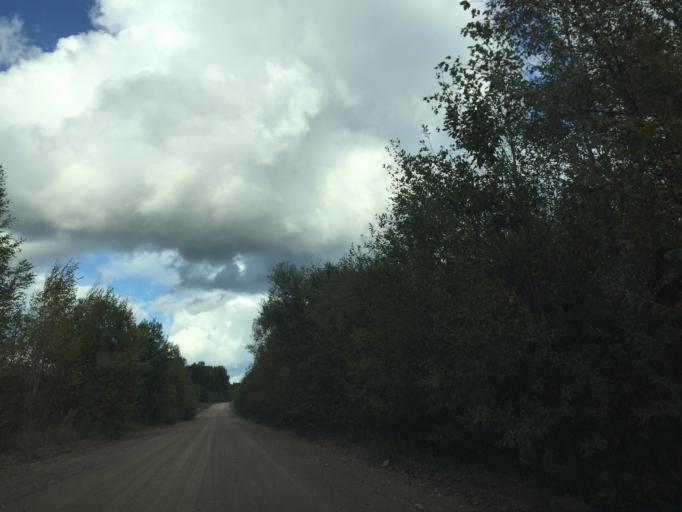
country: LV
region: Malpils
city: Malpils
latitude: 57.0501
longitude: 25.1187
